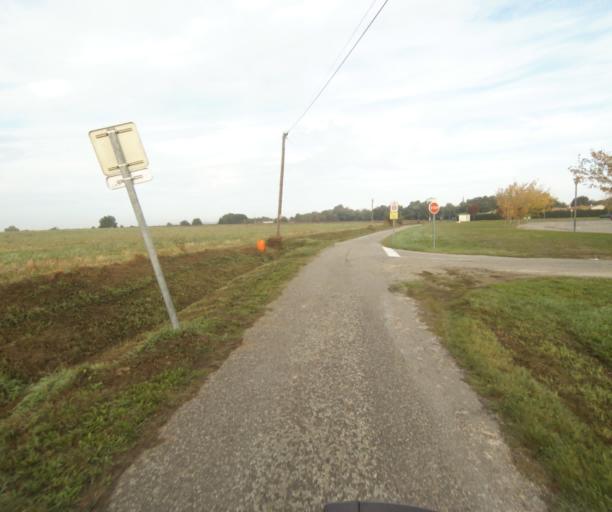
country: FR
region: Midi-Pyrenees
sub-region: Departement du Tarn-et-Garonne
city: Montech
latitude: 43.9490
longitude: 1.2386
